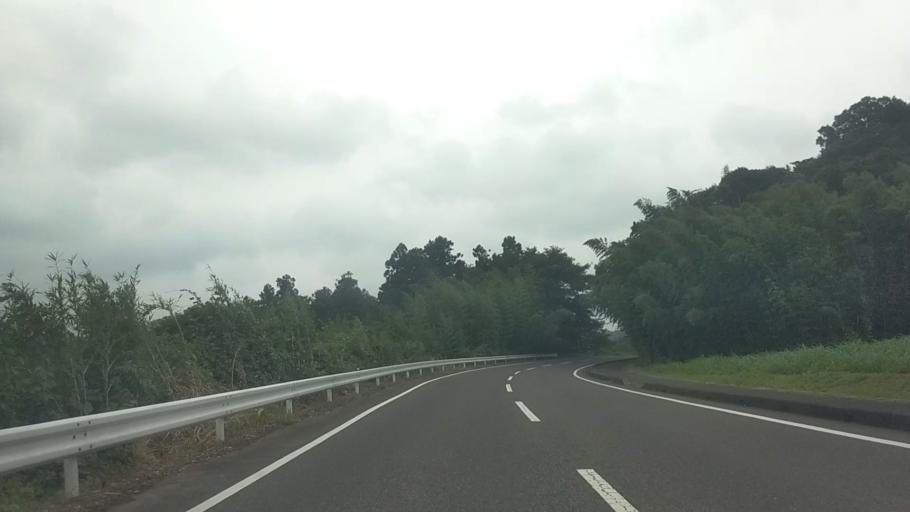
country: JP
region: Chiba
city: Kimitsu
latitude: 35.2199
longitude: 139.9140
